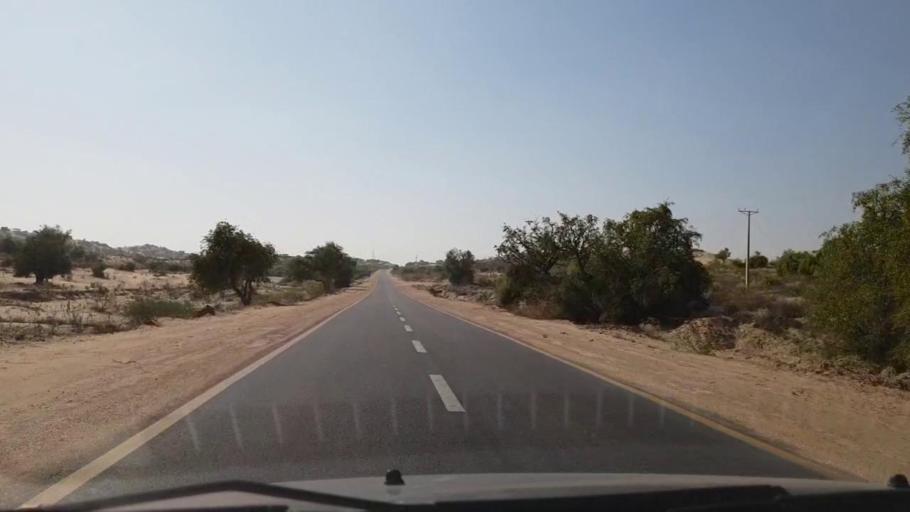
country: PK
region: Sindh
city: Diplo
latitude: 24.4962
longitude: 69.6019
